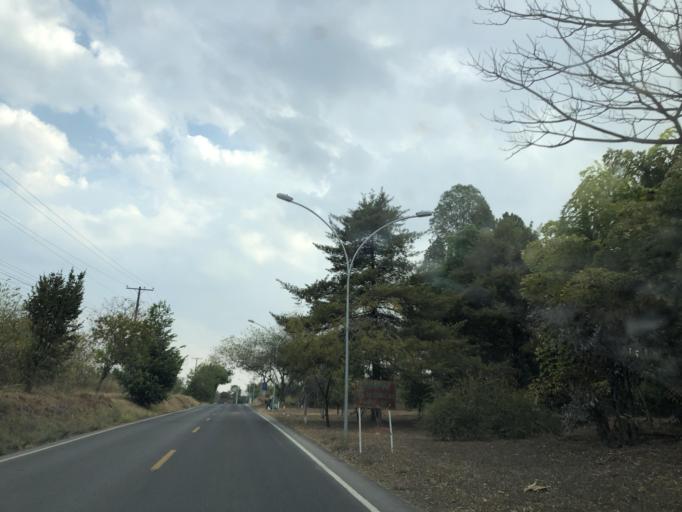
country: BR
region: Federal District
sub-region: Brasilia
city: Brasilia
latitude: -15.9364
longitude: -47.9744
